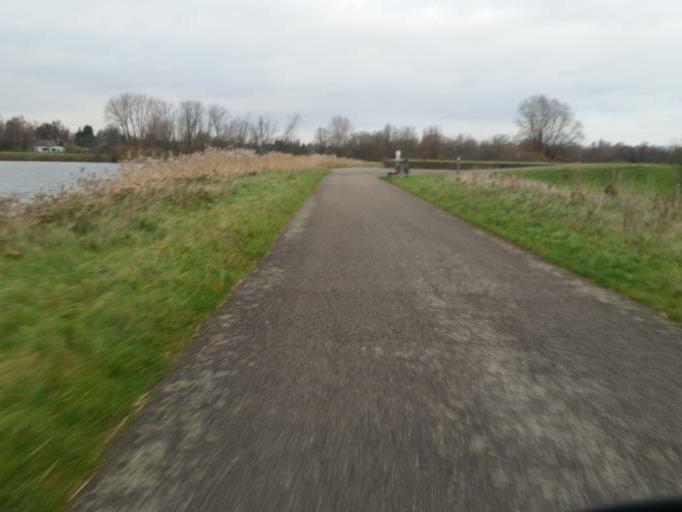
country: BE
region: Flanders
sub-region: Provincie Antwerpen
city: Lier
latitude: 51.1494
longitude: 4.5852
